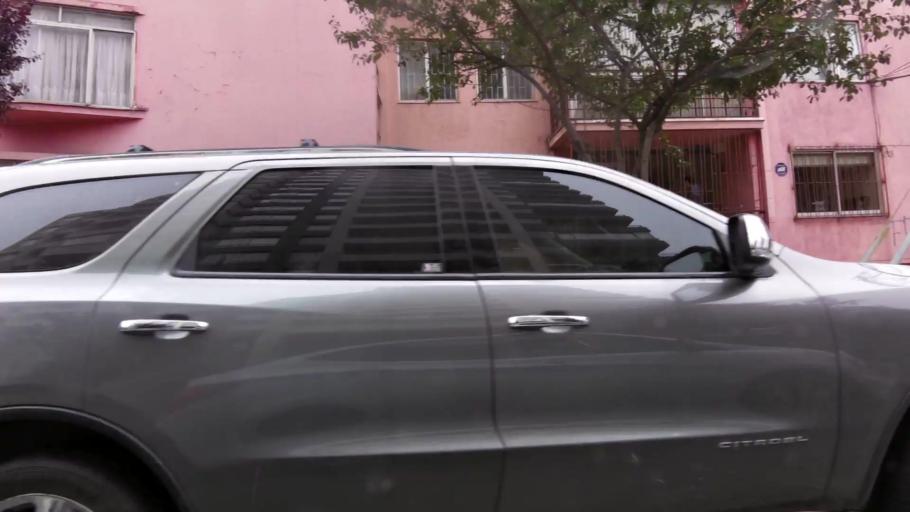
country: CL
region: Biobio
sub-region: Provincia de Concepcion
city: Concepcion
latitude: -36.8288
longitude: -73.0436
